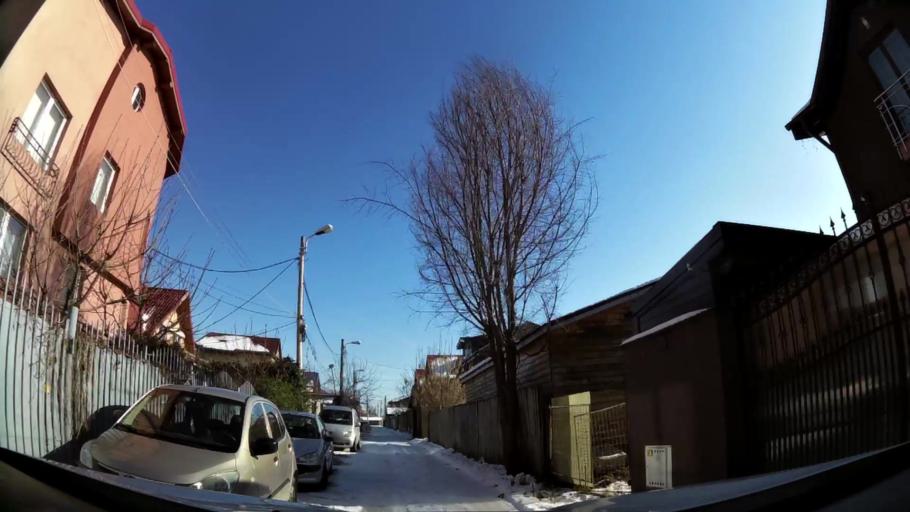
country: RO
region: Ilfov
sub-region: Comuna Magurele
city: Magurele
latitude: 44.3975
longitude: 26.0505
